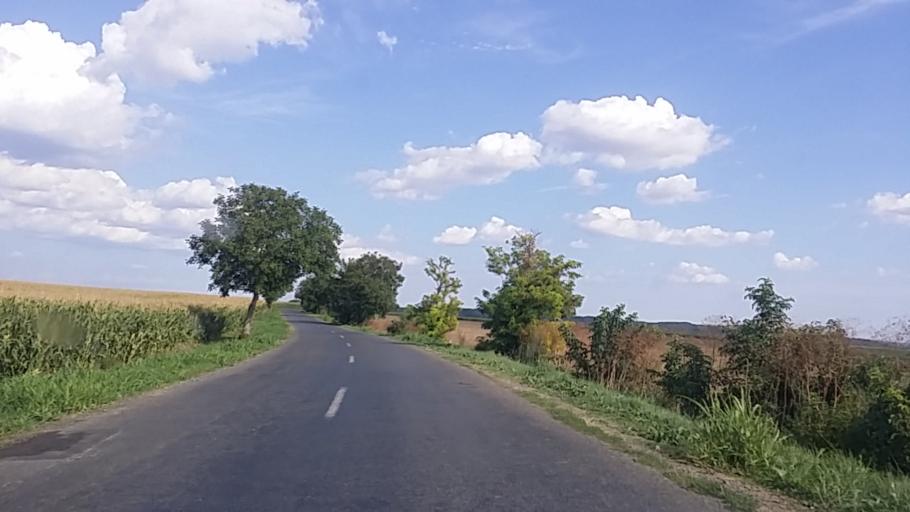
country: HU
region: Tolna
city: Gyonk
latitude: 46.5112
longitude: 18.5432
